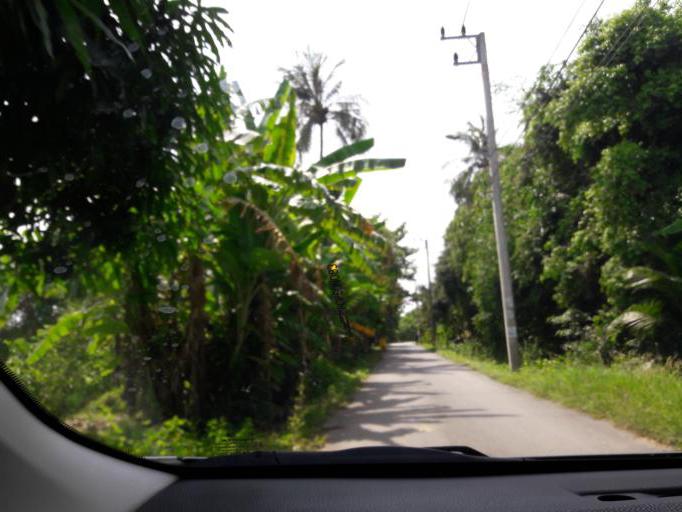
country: TH
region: Ang Thong
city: Ang Thong
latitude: 14.5750
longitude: 100.4413
